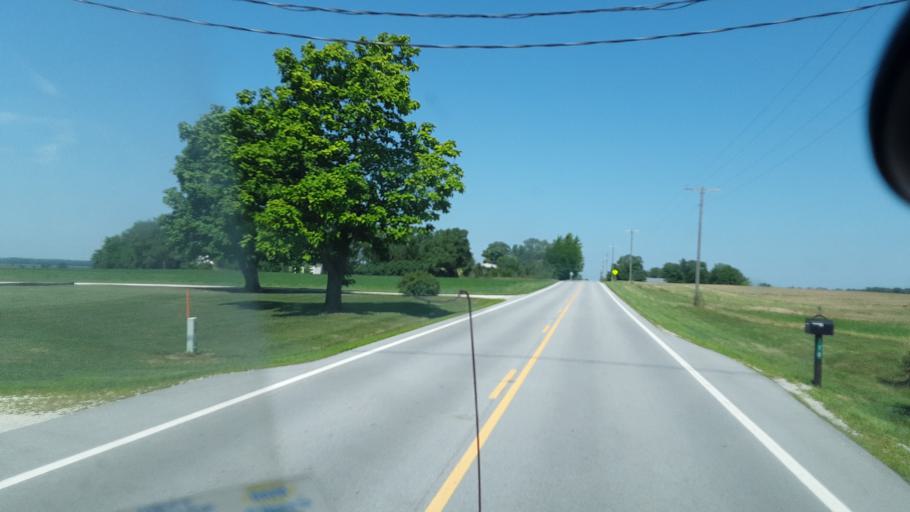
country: US
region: Ohio
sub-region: Wyandot County
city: Carey
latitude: 40.9851
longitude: -83.4502
